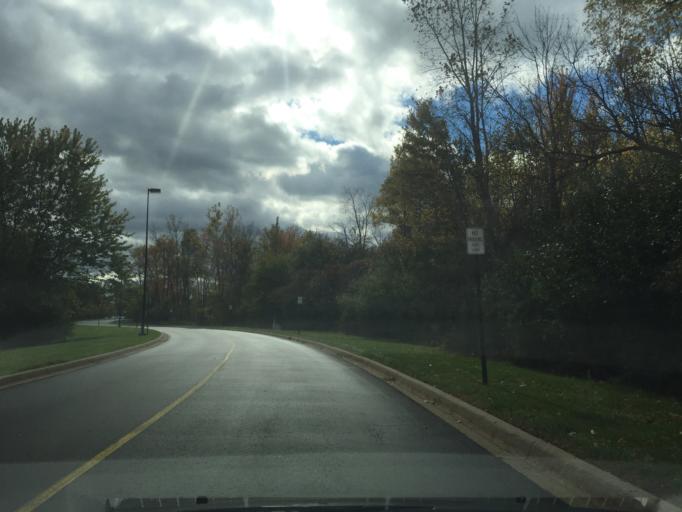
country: US
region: Michigan
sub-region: Oakland County
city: Auburn Hills
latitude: 42.6480
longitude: -83.2349
